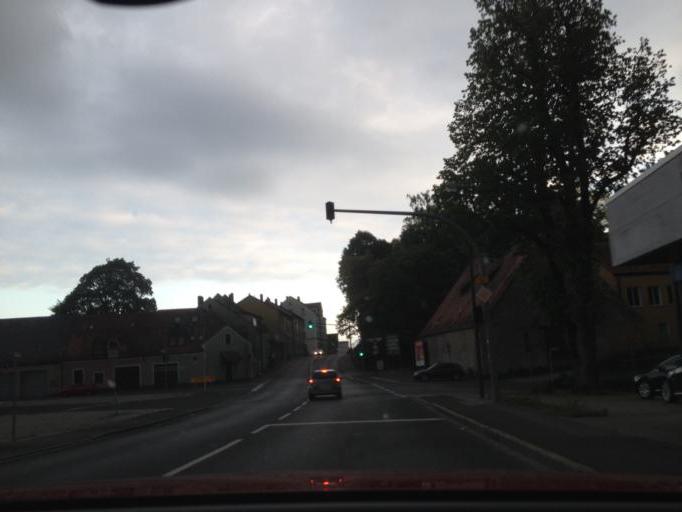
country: DE
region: Bavaria
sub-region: Upper Palatinate
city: Sulzbach-Rosenberg
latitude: 49.5072
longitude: 11.7440
